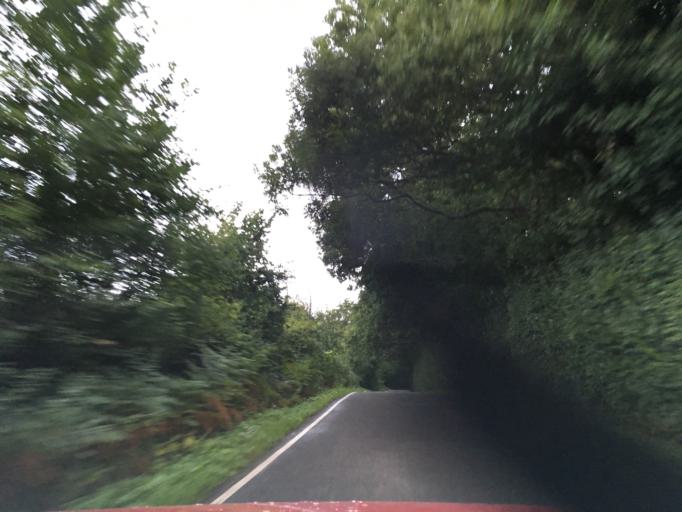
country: GB
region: Wales
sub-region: Monmouthshire
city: Llangwm
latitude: 51.6566
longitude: -2.8553
